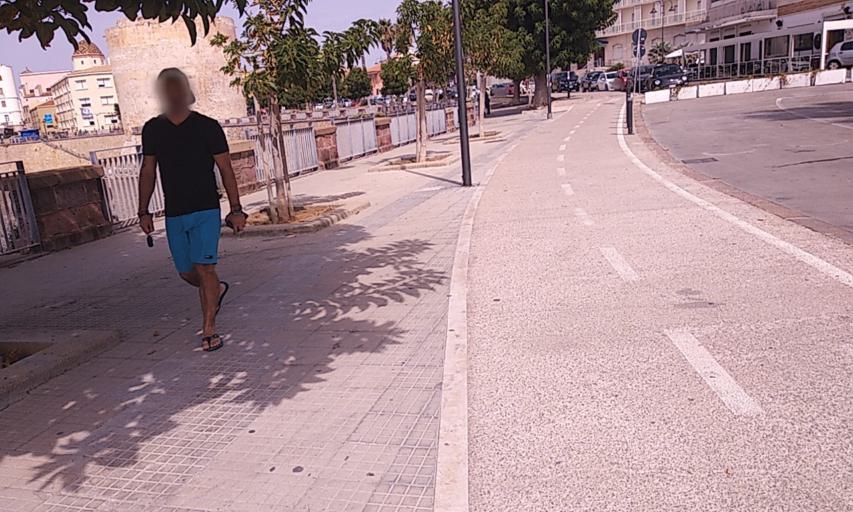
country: IT
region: Sardinia
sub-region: Provincia di Sassari
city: Alghero
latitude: 40.5549
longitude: 8.3156
